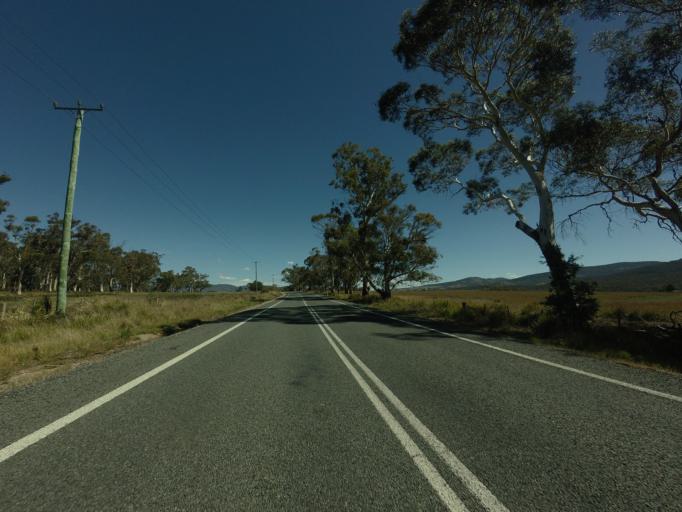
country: AU
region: Tasmania
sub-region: Northern Midlands
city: Evandale
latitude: -41.7572
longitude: 147.7550
